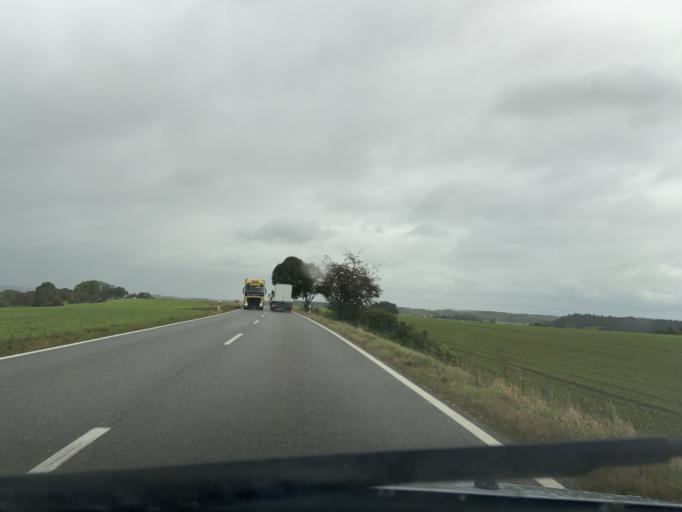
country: DE
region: Baden-Wuerttemberg
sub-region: Tuebingen Region
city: Krauchenwies
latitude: 48.0232
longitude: 9.2725
